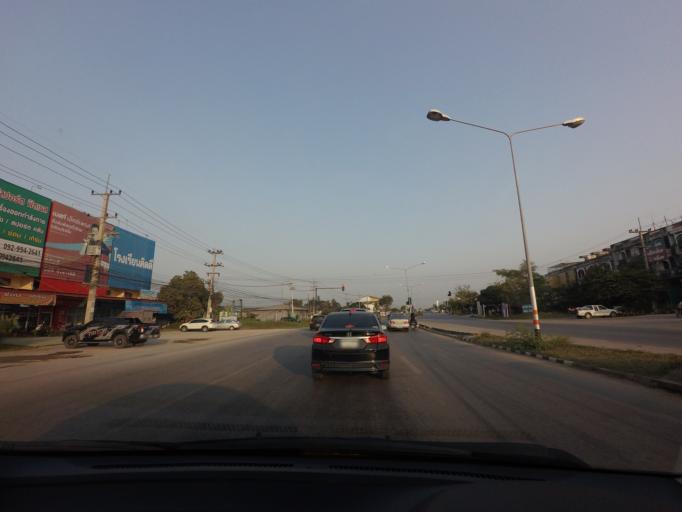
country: TH
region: Sukhothai
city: Sukhothai
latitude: 17.0224
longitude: 99.8160
